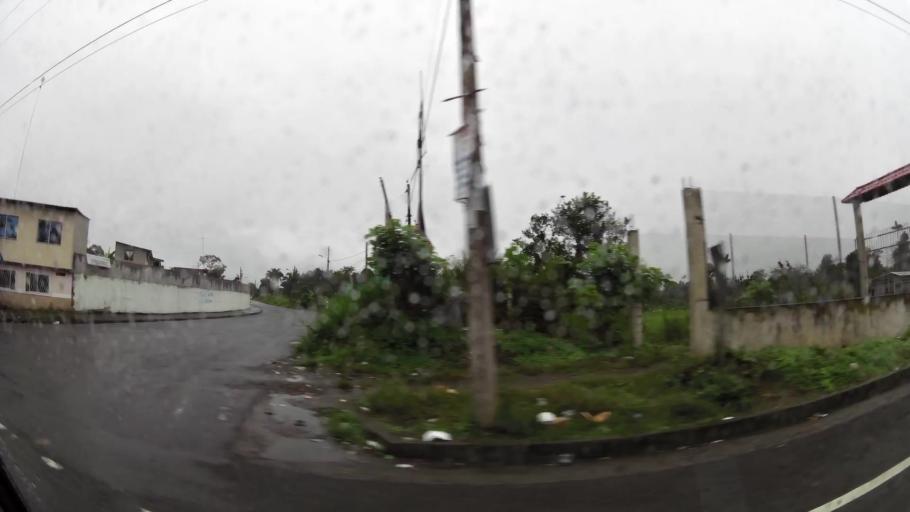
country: EC
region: Santo Domingo de los Tsachilas
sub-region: Canton Santo Domingo de los Colorados
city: Santo Domingo de los Colorados
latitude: -0.2346
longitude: -79.1277
